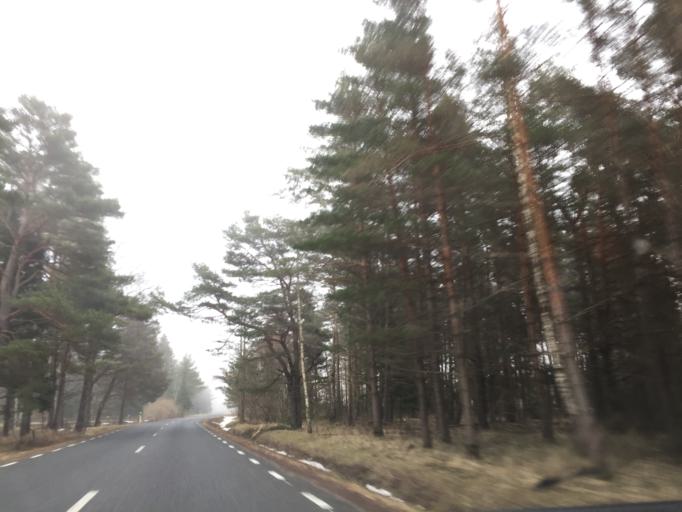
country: EE
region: Saare
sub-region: Kuressaare linn
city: Kuressaare
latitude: 58.4669
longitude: 22.0150
